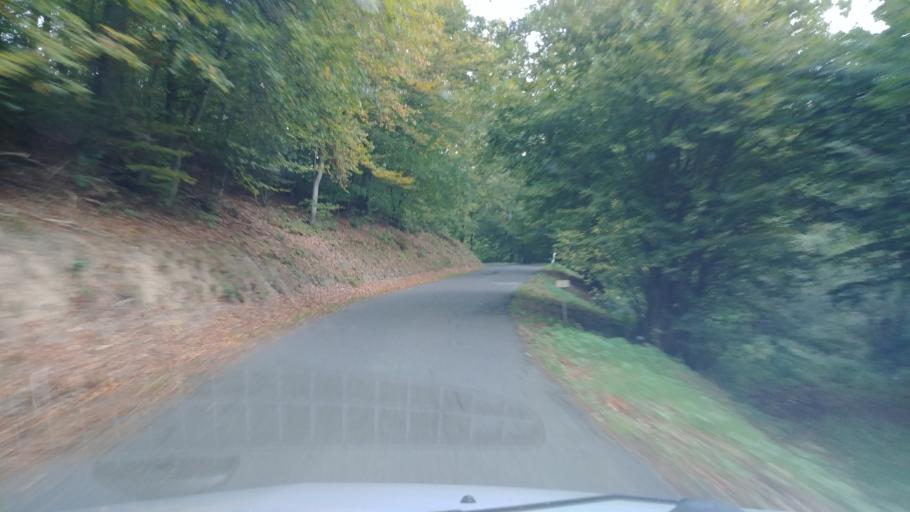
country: DE
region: Rheinland-Pfalz
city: Merschbach
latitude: 49.8110
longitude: 7.0093
